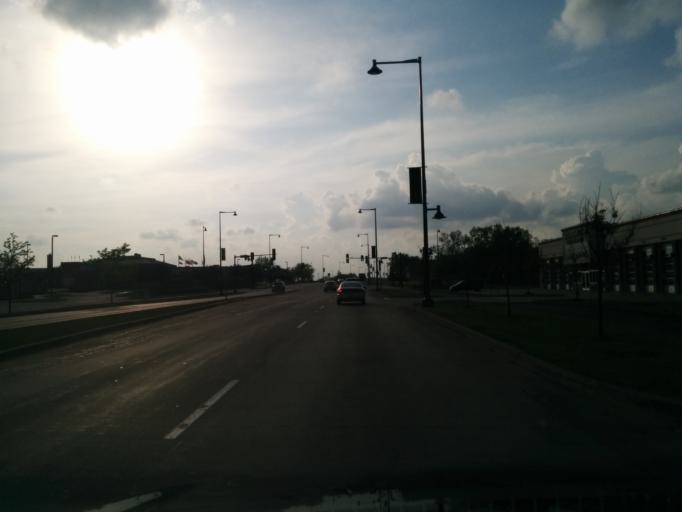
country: US
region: Illinois
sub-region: DuPage County
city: Hanover Park
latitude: 41.9902
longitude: -88.1564
